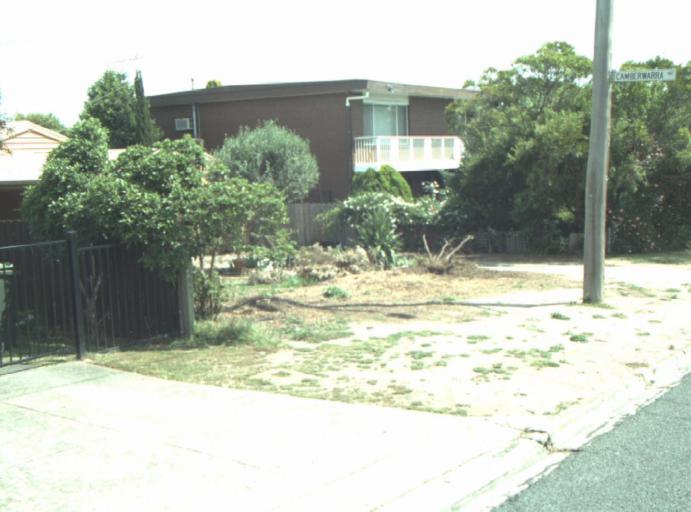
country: AU
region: Victoria
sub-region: Greater Geelong
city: Clifton Springs
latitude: -38.1466
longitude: 144.5759
